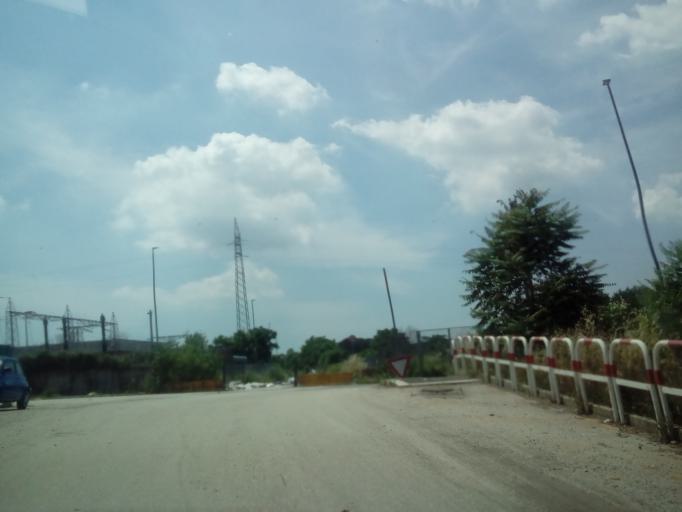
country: IT
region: Latium
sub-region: Citta metropolitana di Roma Capitale
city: Colle Verde
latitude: 41.9306
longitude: 12.5905
